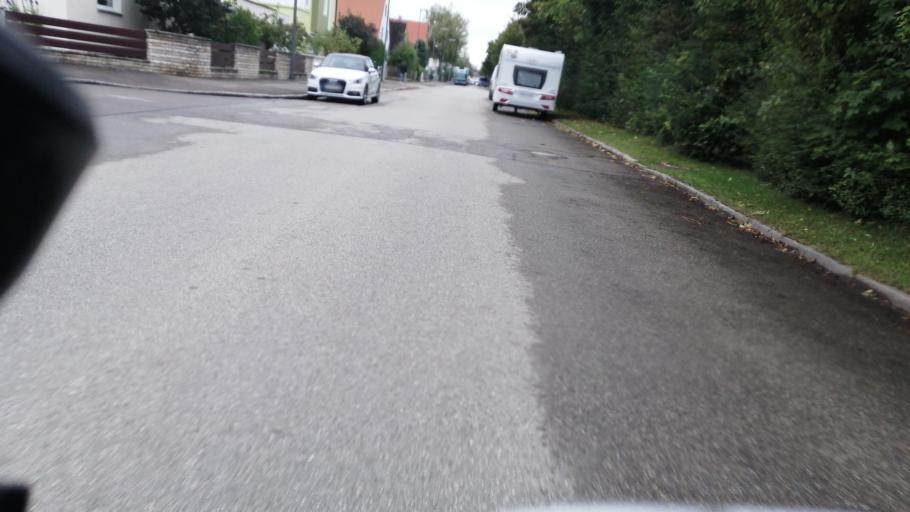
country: DE
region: Bavaria
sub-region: Upper Bavaria
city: Unterfoehring
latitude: 48.2068
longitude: 11.5943
